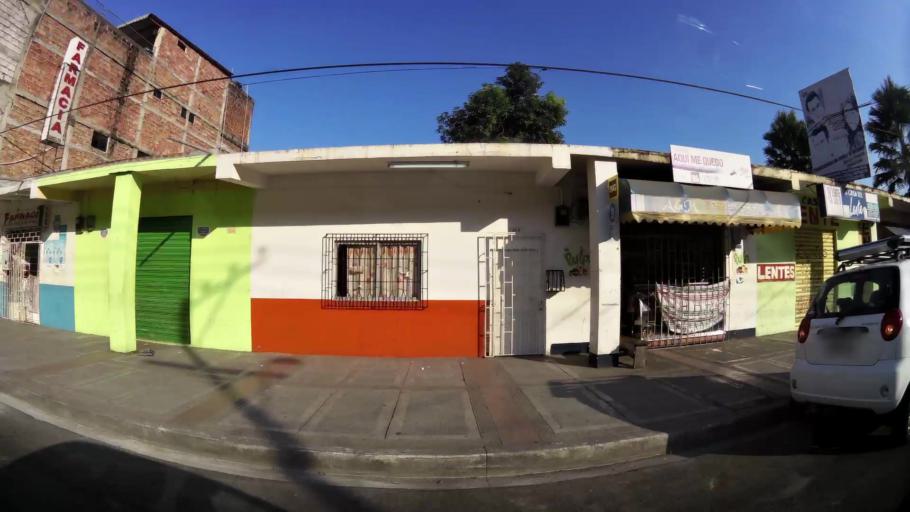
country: EC
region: Guayas
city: Eloy Alfaro
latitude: -2.1742
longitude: -79.8529
